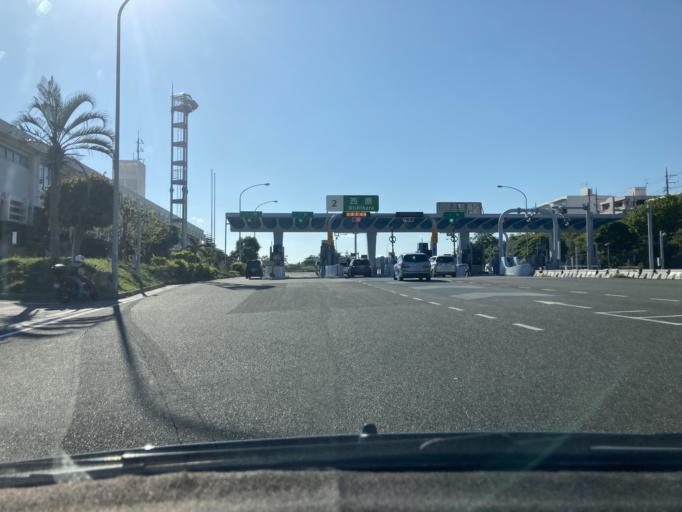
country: JP
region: Okinawa
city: Ginowan
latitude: 26.2486
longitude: 127.7492
